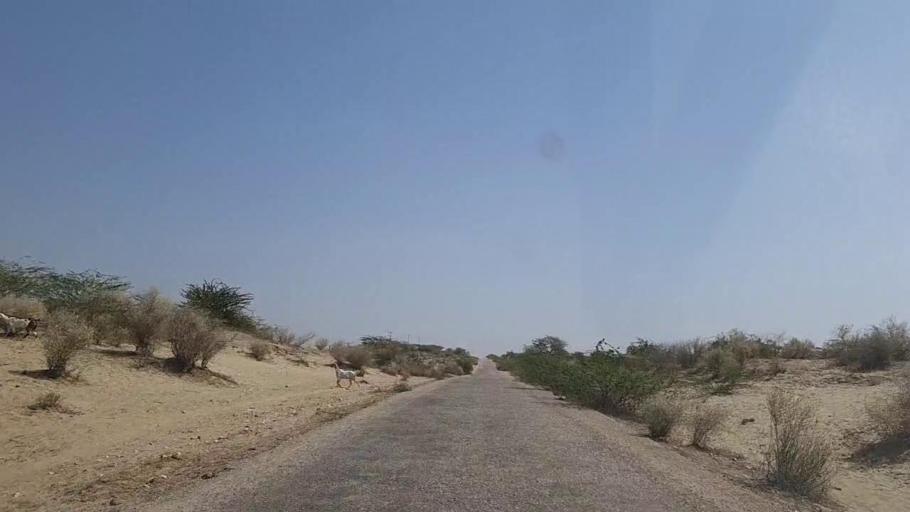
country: PK
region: Sindh
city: Diplo
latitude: 24.5142
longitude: 69.3852
